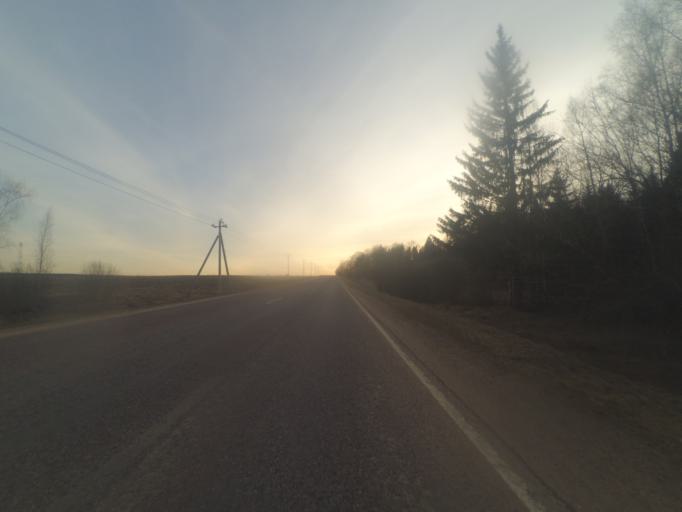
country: RU
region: Moskovskaya
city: Karinskoye
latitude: 55.7750
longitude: 36.5968
